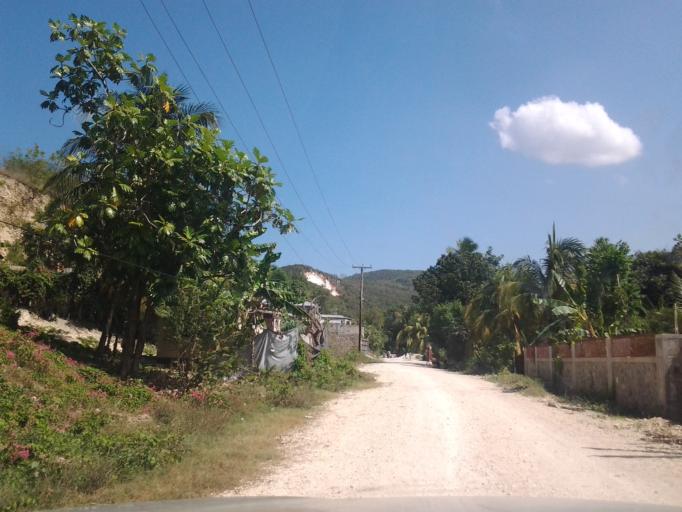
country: HT
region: Ouest
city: Tigwav
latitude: 18.4401
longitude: -72.8411
